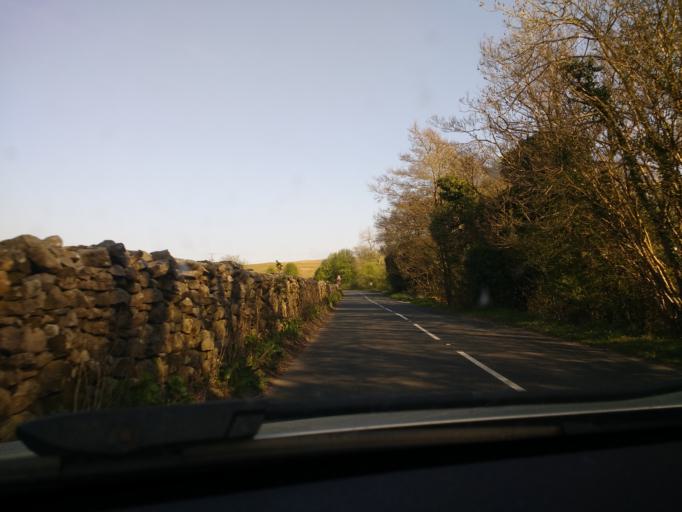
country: GB
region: England
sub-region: Cumbria
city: Sedbergh
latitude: 54.3172
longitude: -2.4857
